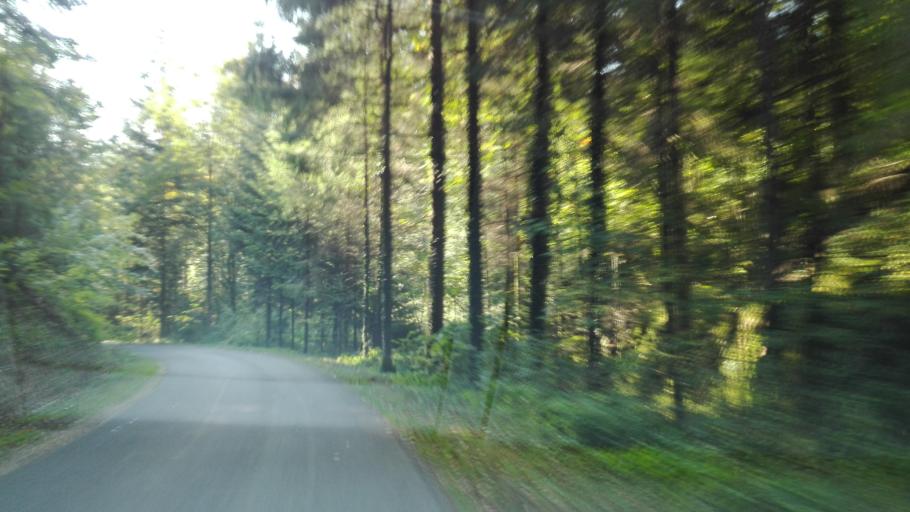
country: AT
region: Upper Austria
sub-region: Politischer Bezirk Perg
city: Perg
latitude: 48.2927
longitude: 14.6039
